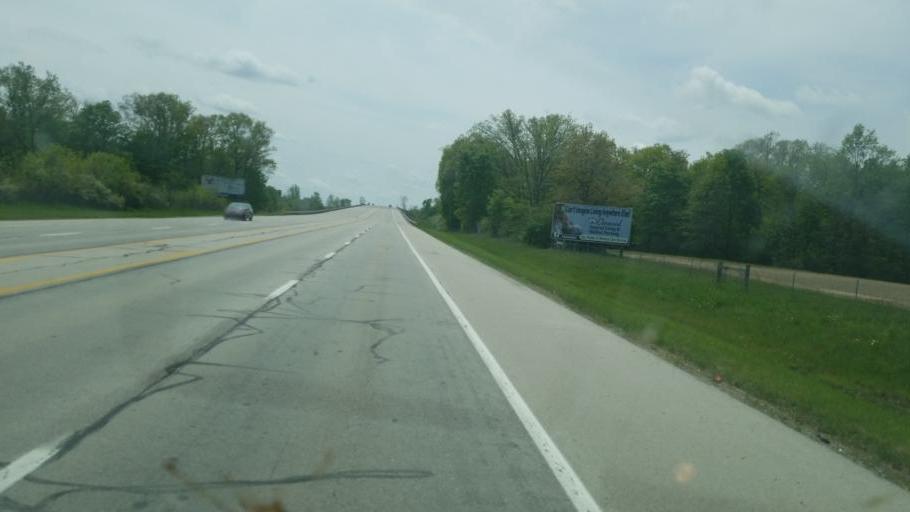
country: US
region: Ohio
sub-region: Sandusky County
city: Fremont
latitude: 41.3896
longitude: -83.1127
